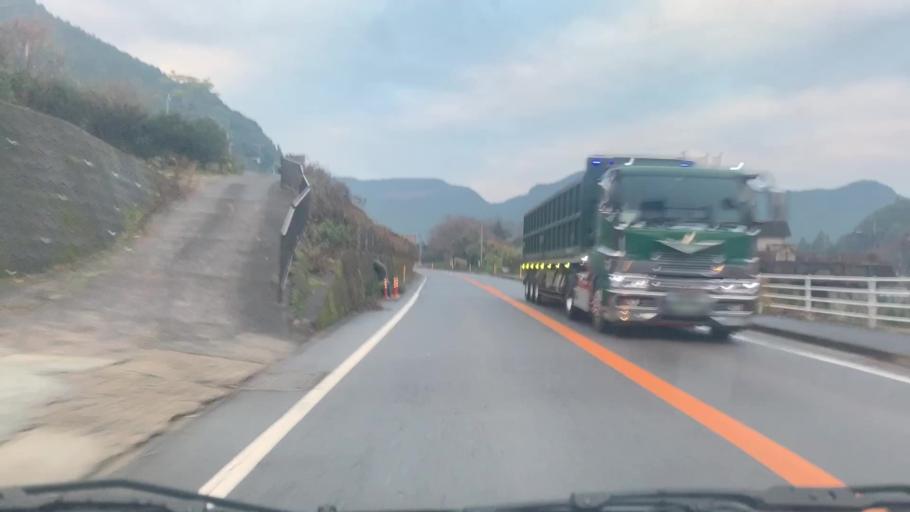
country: JP
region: Saga Prefecture
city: Ureshinomachi-shimojuku
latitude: 33.0790
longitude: 129.9679
